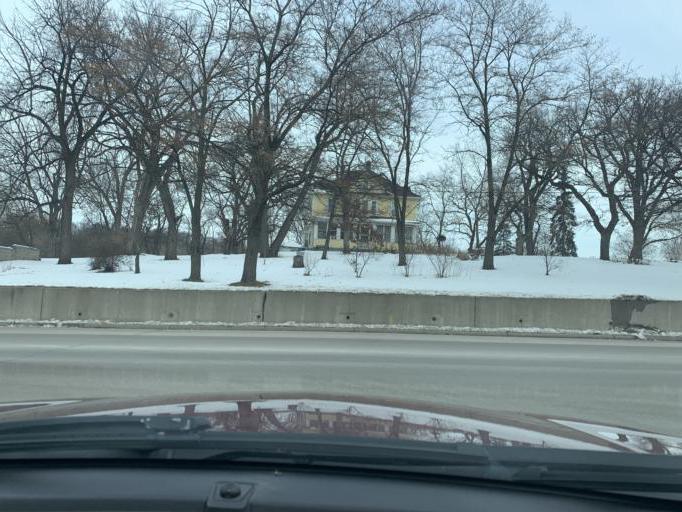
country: US
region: Minnesota
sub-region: Washington County
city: Saint Paul Park
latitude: 44.8460
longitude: -92.9872
